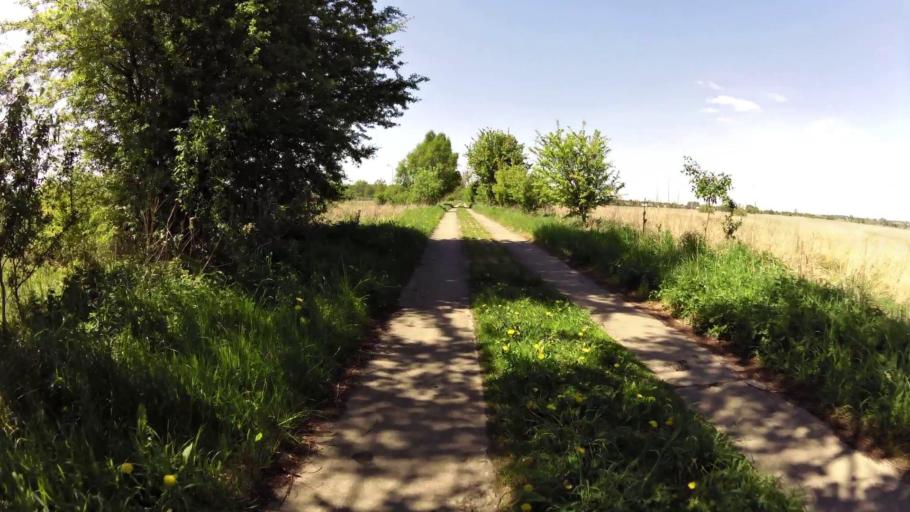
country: PL
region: West Pomeranian Voivodeship
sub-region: Powiat bialogardzki
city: Bialogard
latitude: 54.0012
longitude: 16.0223
